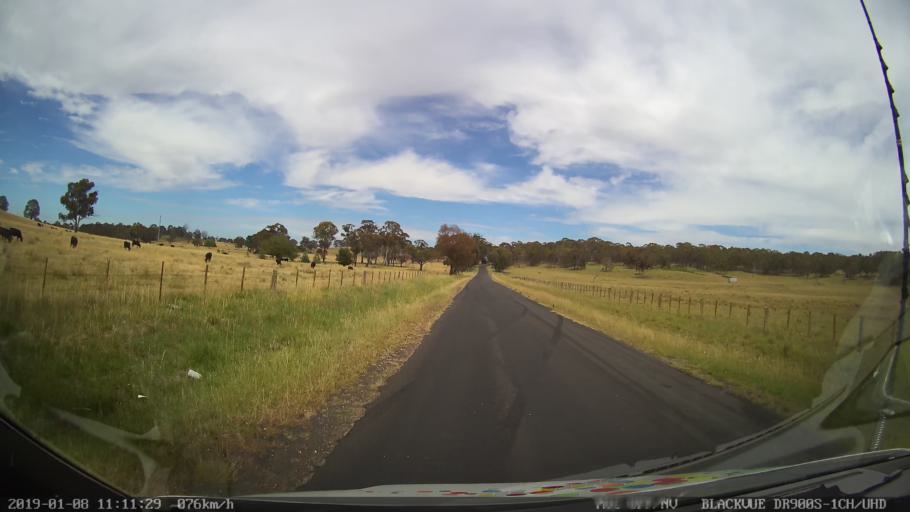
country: AU
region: New South Wales
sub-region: Guyra
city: Guyra
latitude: -30.2263
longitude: 151.6236
